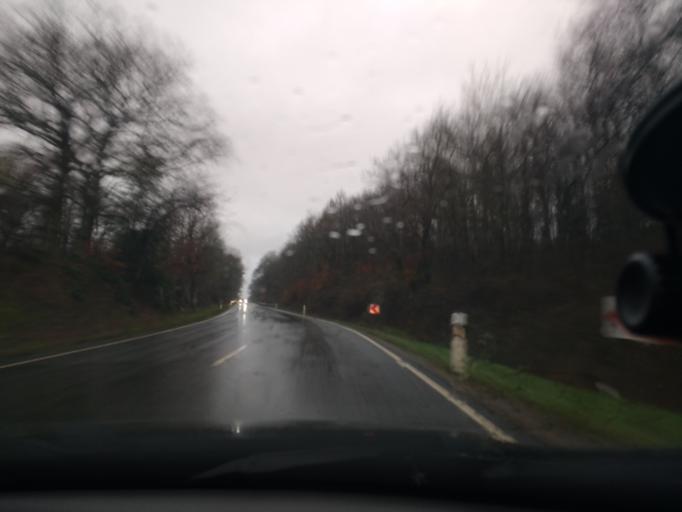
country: DE
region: Rheinland-Pfalz
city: Pellingen
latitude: 49.6990
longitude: 6.6415
